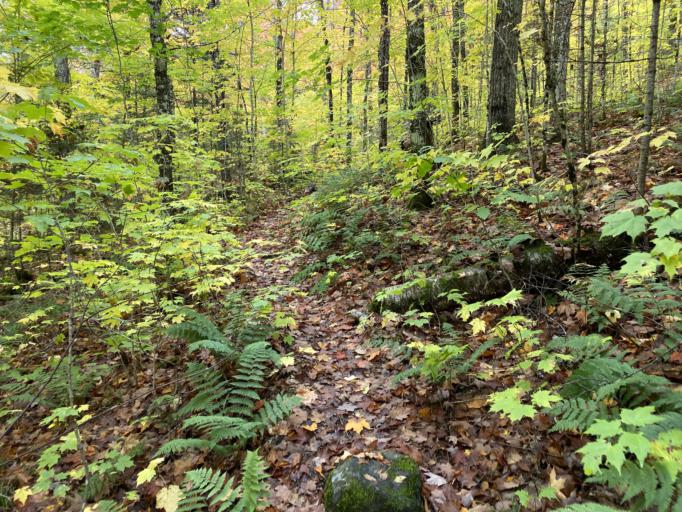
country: US
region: Michigan
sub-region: Marquette County
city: West Ishpeming
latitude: 46.5407
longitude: -87.9975
